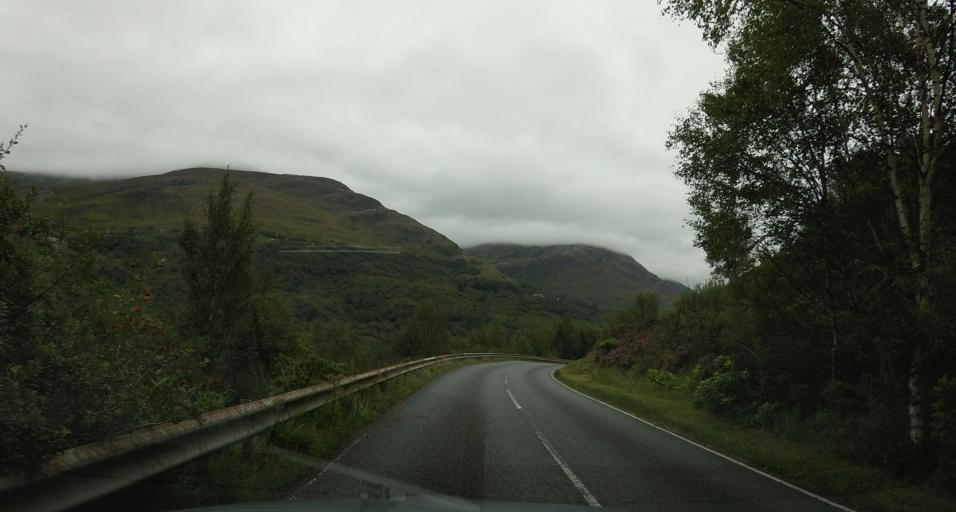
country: GB
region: Scotland
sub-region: Highland
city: Fort William
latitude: 56.7112
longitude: -4.9831
